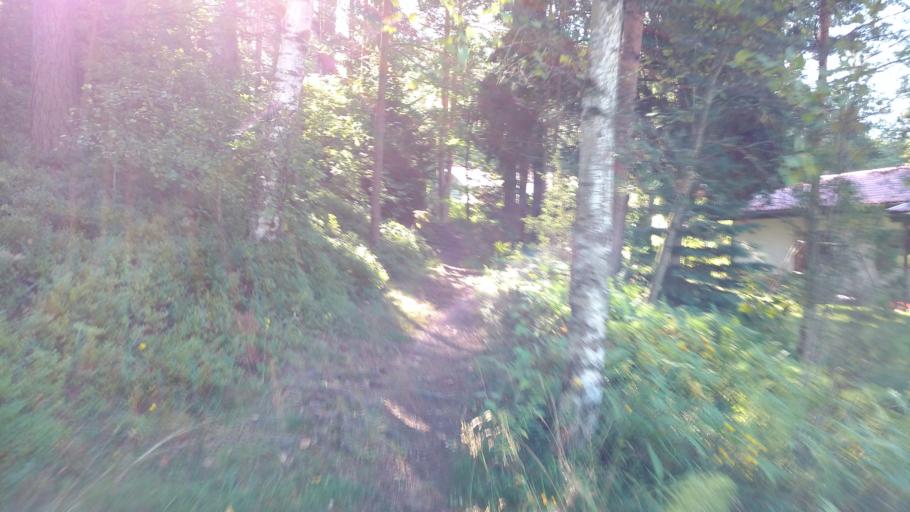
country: FI
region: Varsinais-Suomi
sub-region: Salo
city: Salo
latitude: 60.3840
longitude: 23.1652
